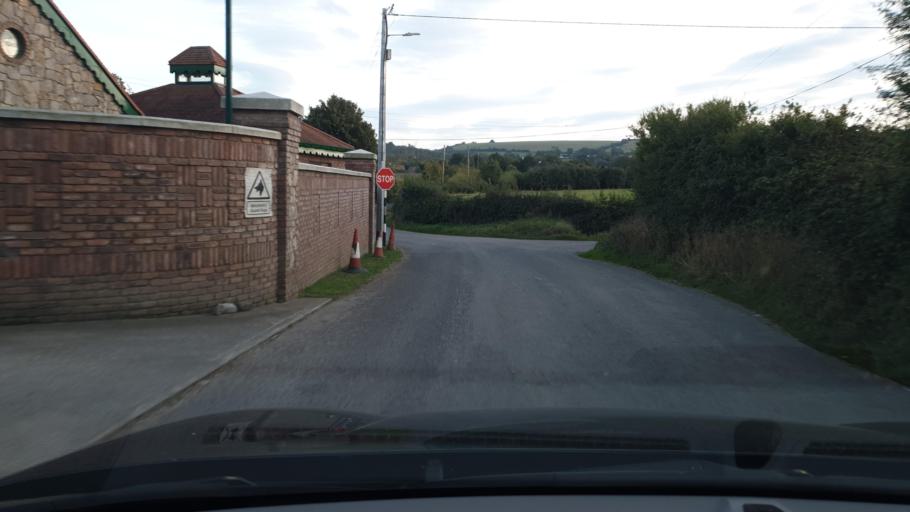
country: IE
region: Leinster
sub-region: An Mhi
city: Stamullin
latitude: 53.5879
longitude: -6.2456
